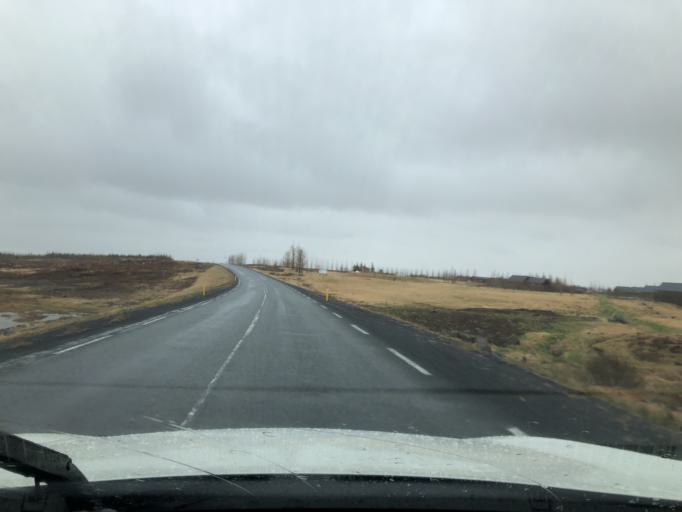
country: IS
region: South
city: Selfoss
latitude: 64.0775
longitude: -20.7561
